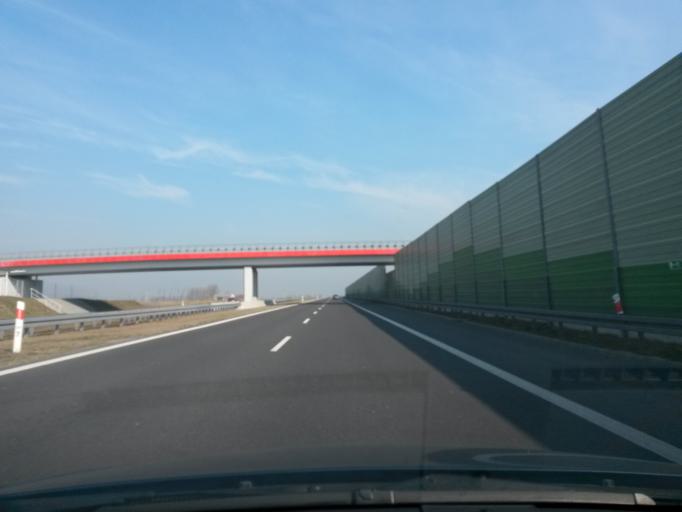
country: PL
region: Lodz Voivodeship
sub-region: Powiat kutnowski
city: Krzyzanow
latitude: 52.1559
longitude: 19.4825
